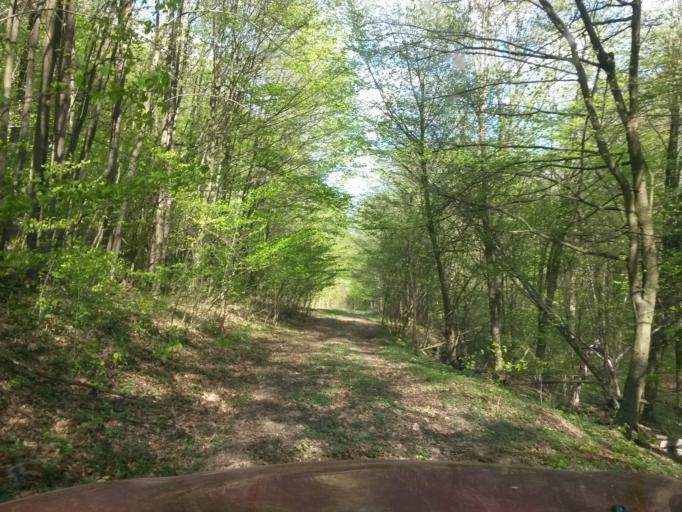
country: SK
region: Presovsky
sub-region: Okres Presov
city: Presov
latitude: 48.9469
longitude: 21.1370
